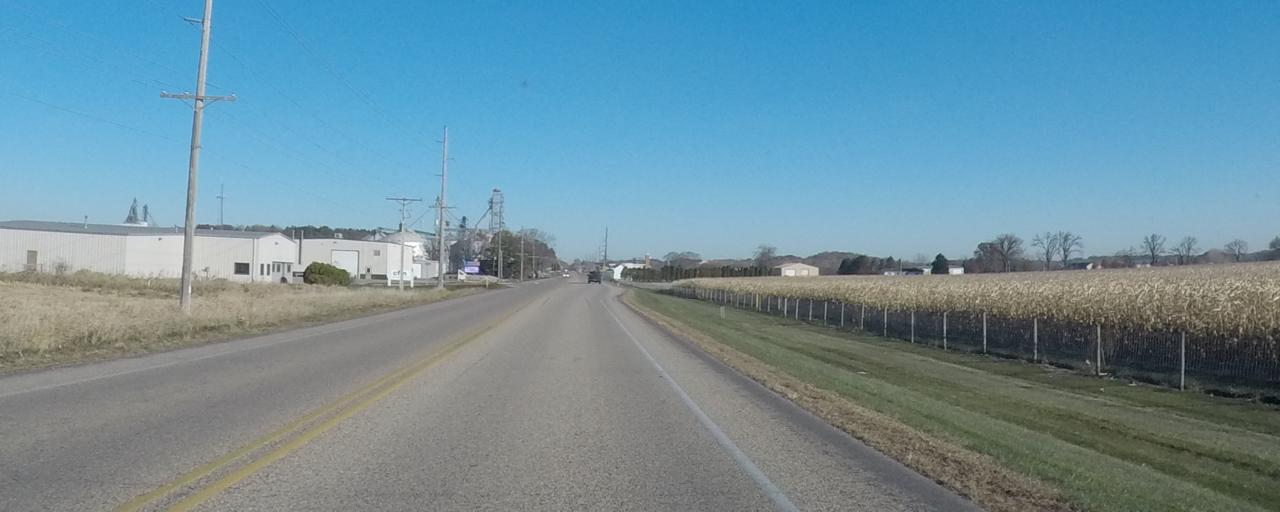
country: US
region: Wisconsin
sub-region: Dane County
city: Cottage Grove
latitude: 43.0605
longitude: -89.1997
